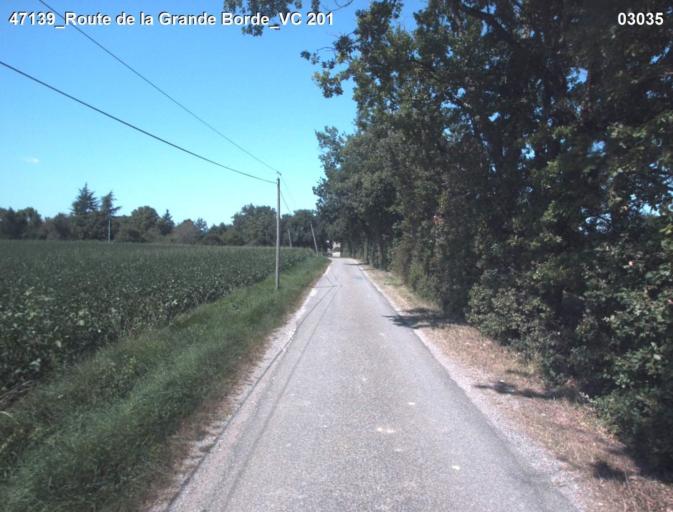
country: FR
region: Aquitaine
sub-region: Departement du Lot-et-Garonne
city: Nerac
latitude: 44.0862
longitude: 0.3815
